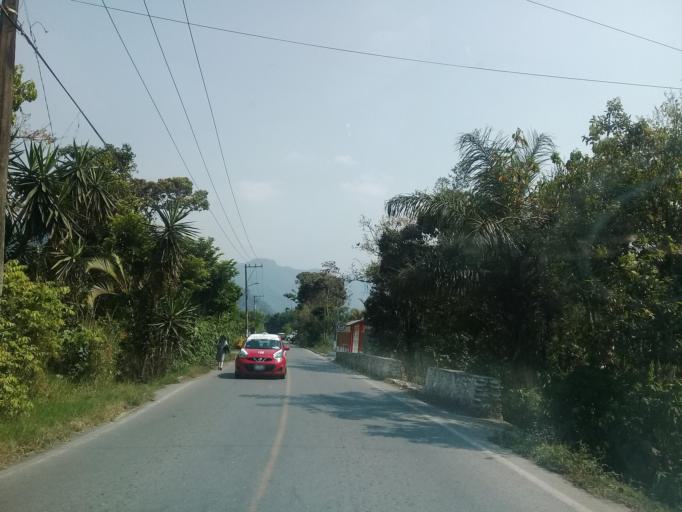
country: MX
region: Veracruz
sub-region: Ixtaczoquitlan
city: Campo Chico
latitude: 18.8268
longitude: -97.0212
